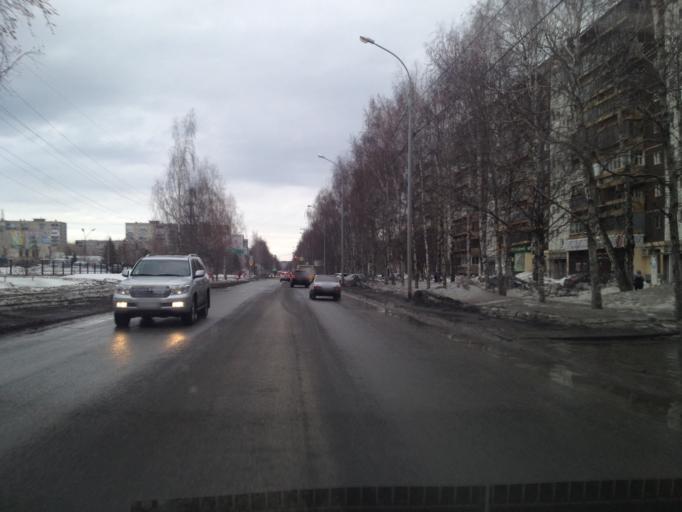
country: RU
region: Sverdlovsk
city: Sovkhoznyy
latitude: 56.8046
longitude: 60.5610
